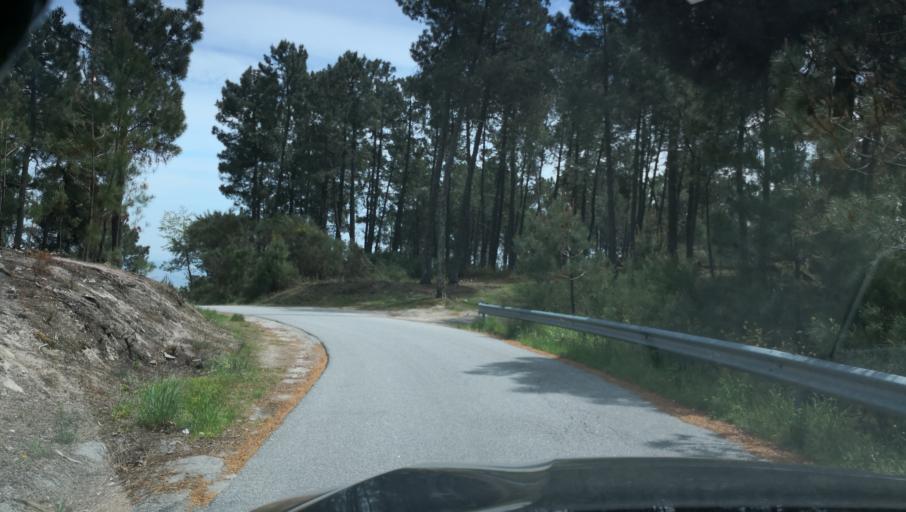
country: PT
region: Vila Real
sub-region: Vila Real
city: Vila Real
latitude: 41.3181
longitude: -7.7899
